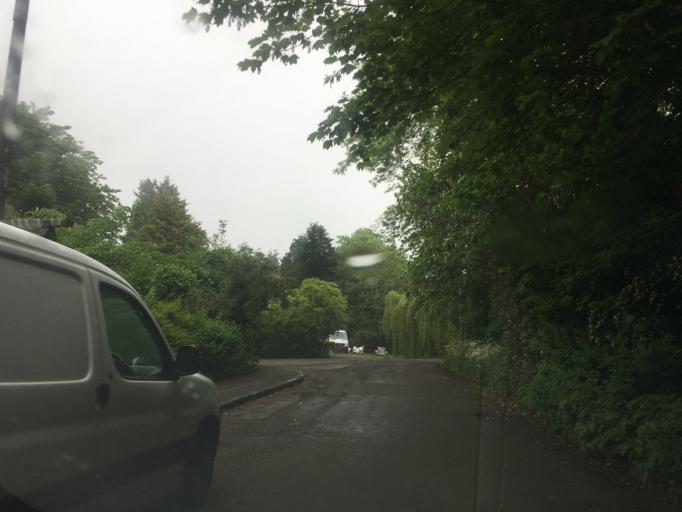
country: GB
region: Scotland
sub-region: Midlothian
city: Loanhead
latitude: 55.8978
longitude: -3.1961
